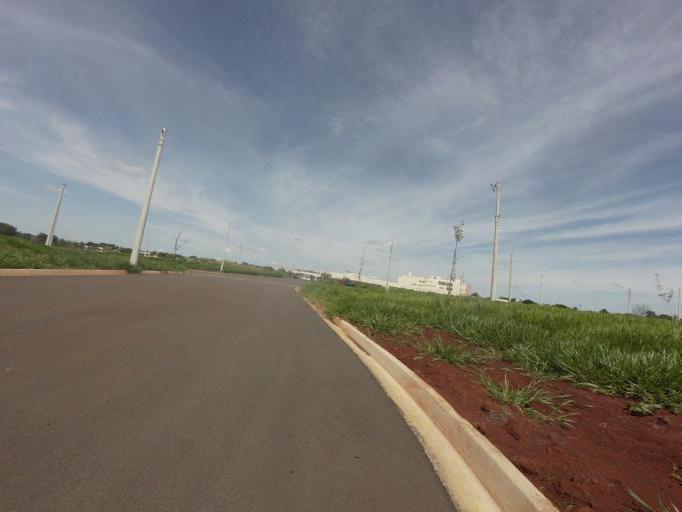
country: BR
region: Sao Paulo
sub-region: Piracicaba
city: Piracicaba
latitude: -22.7610
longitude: -47.5808
